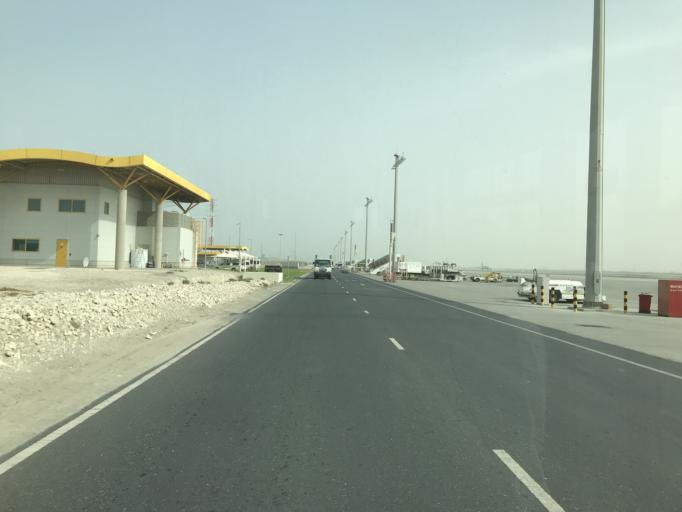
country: QA
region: Baladiyat ad Dawhah
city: Doha
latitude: 25.2785
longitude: 51.5991
